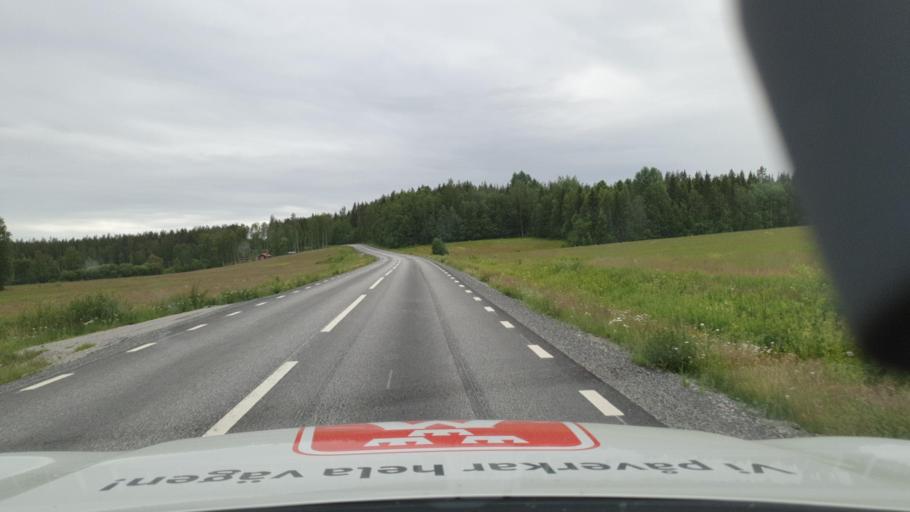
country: SE
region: Vaesterbotten
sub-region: Nordmalings Kommun
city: Nordmaling
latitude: 63.7167
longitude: 19.6361
